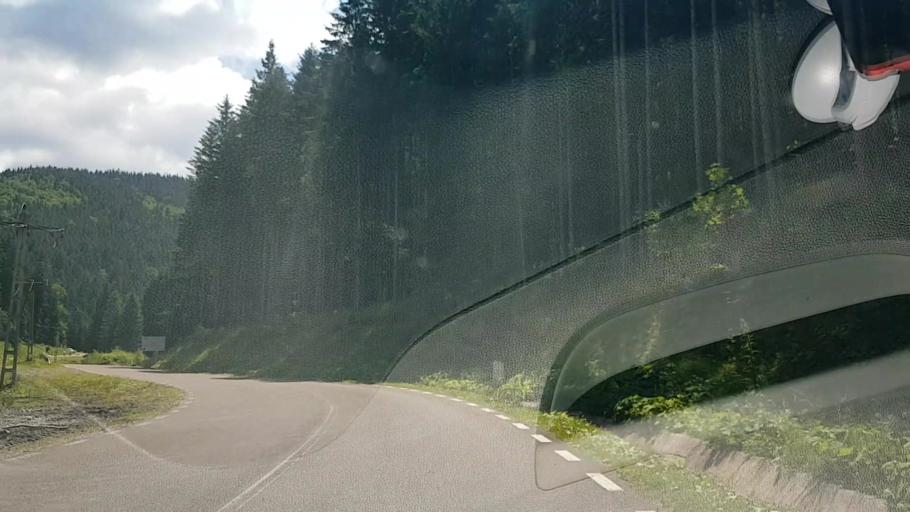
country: RO
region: Suceava
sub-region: Comuna Sadova
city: Sadova
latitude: 47.4725
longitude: 25.5053
